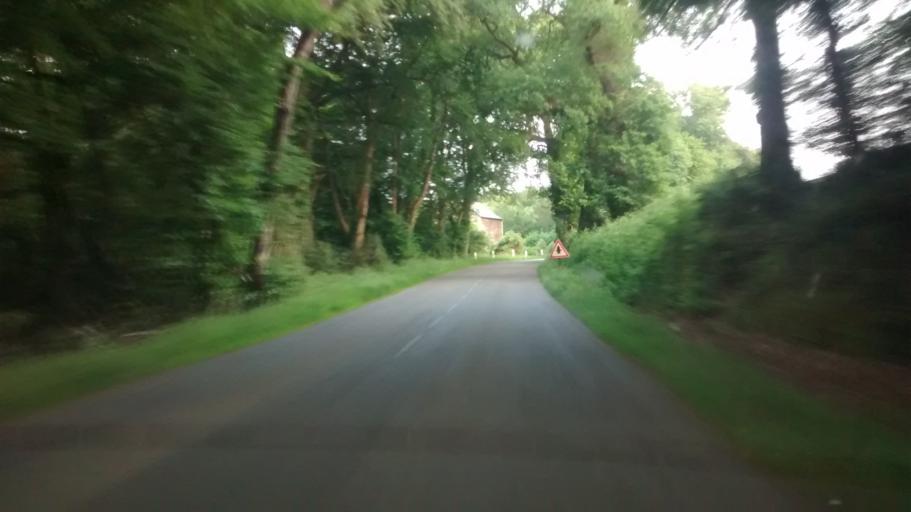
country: FR
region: Brittany
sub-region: Departement du Morbihan
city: Beignon
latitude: 47.9876
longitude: -2.1436
